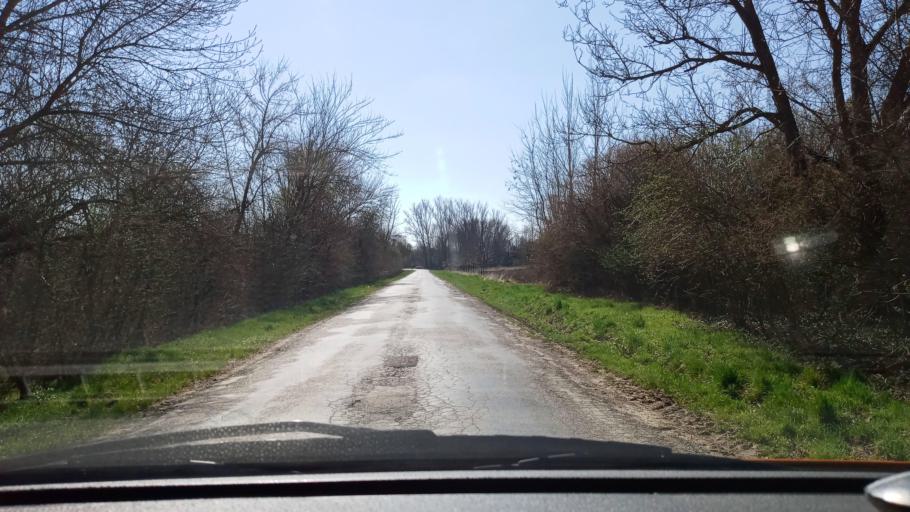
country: HU
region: Baranya
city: Kozarmisleny
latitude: 46.0695
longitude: 18.3661
